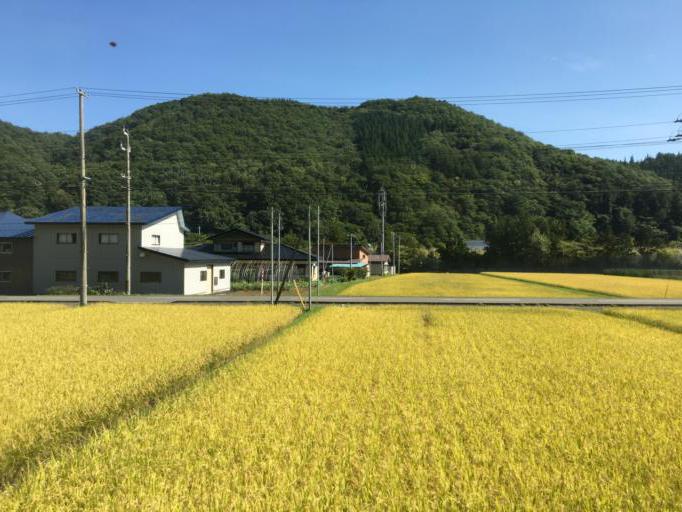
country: JP
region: Akita
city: Hanawa
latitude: 40.0750
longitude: 141.0201
